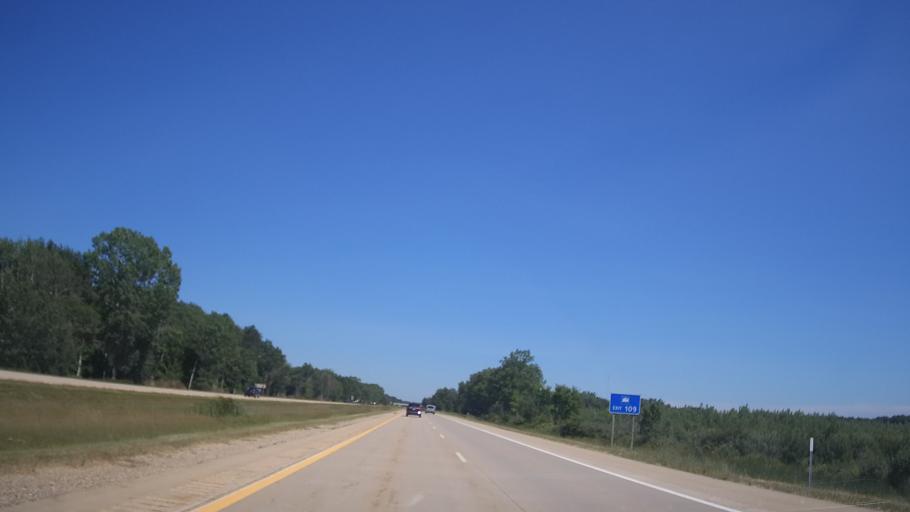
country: US
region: Michigan
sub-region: Midland County
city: Coleman
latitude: 43.7362
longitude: -84.5057
